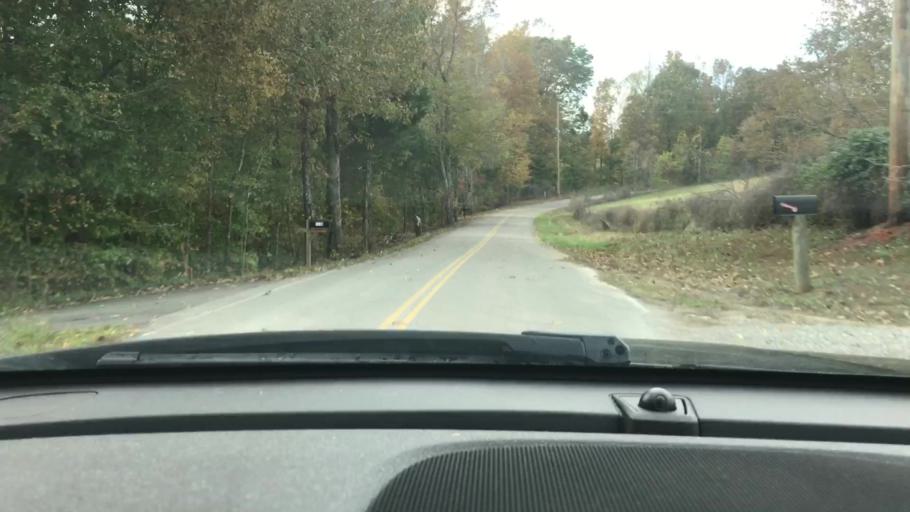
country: US
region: Tennessee
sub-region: Dickson County
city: Charlotte
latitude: 36.1936
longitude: -87.2917
